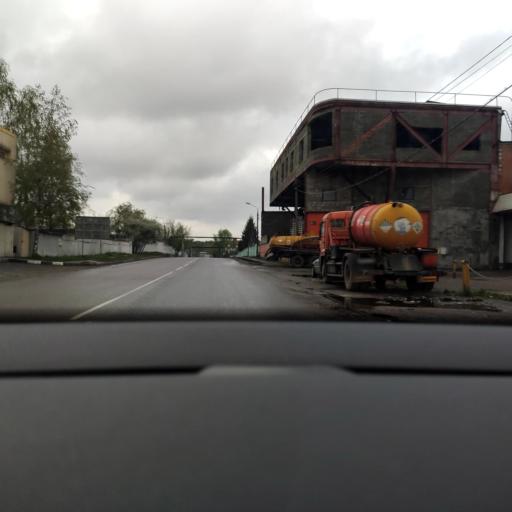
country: RU
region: Moskovskaya
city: Reutov
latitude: 55.7683
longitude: 37.8802
